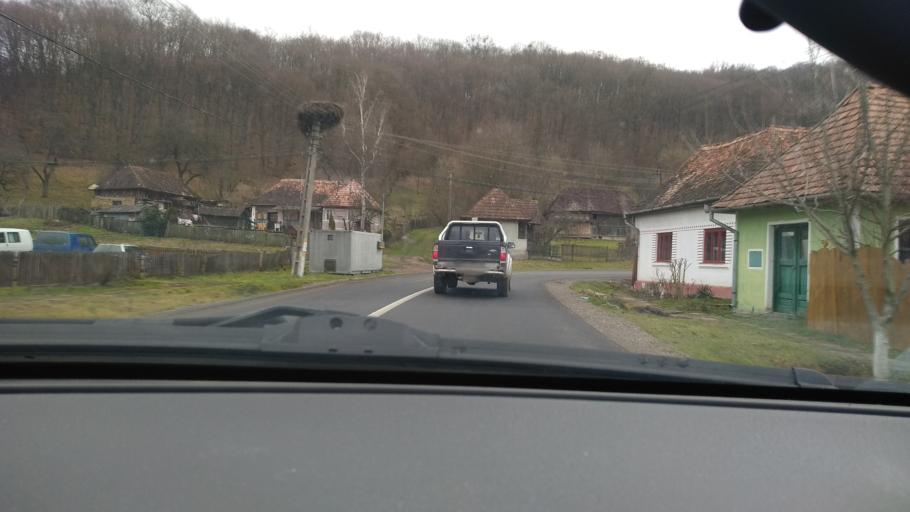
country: RO
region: Mures
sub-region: Comuna Bereni
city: Bereni
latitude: 46.5559
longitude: 24.8680
